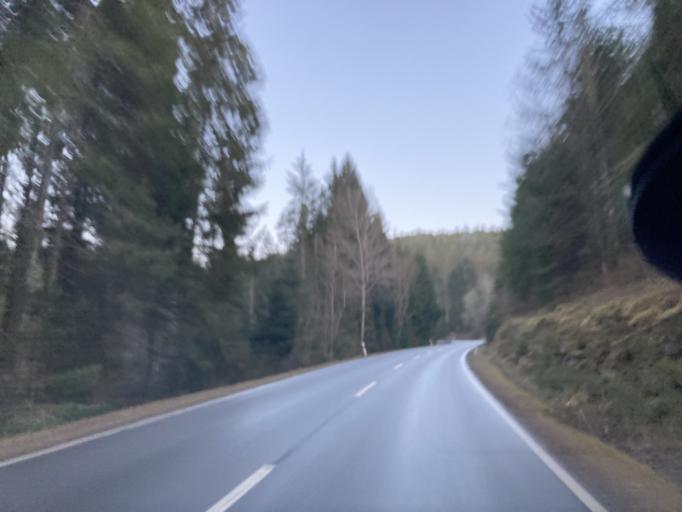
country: DE
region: Baden-Wuerttemberg
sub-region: Karlsruhe Region
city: Neuweiler
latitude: 48.6862
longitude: 8.5747
